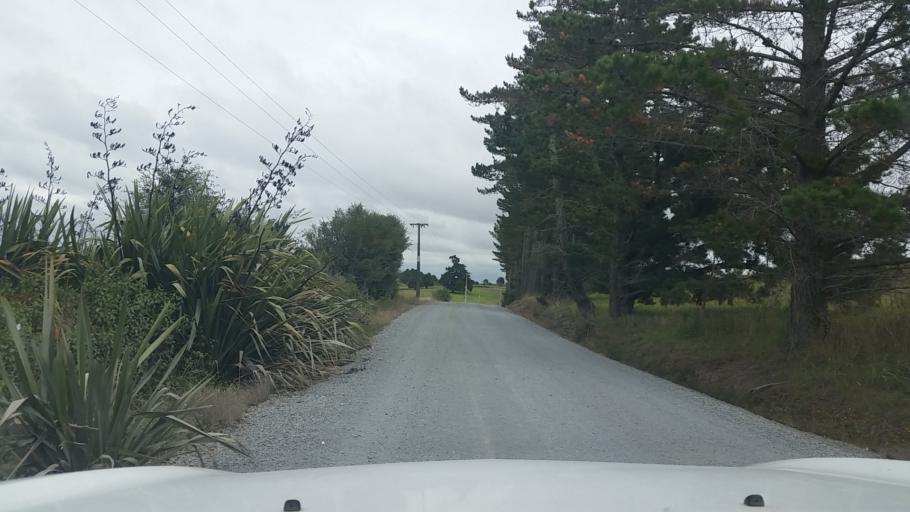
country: NZ
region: Northland
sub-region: Whangarei
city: Maungatapere
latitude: -35.6632
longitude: 174.1845
